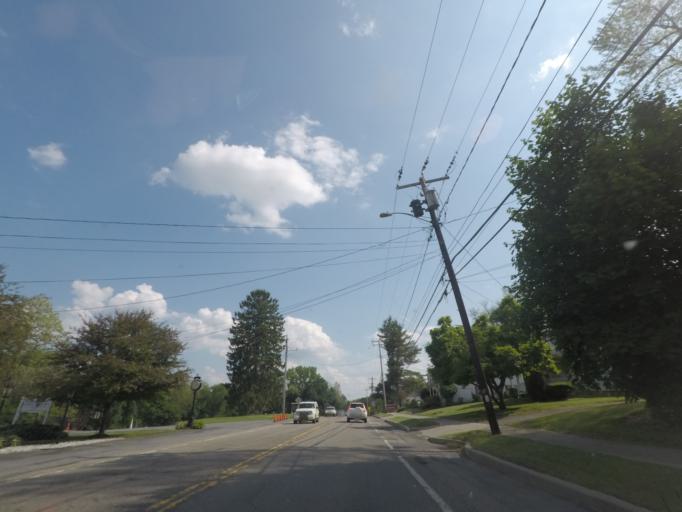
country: US
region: New York
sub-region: Ulster County
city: Marlboro
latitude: 41.6035
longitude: -73.9724
